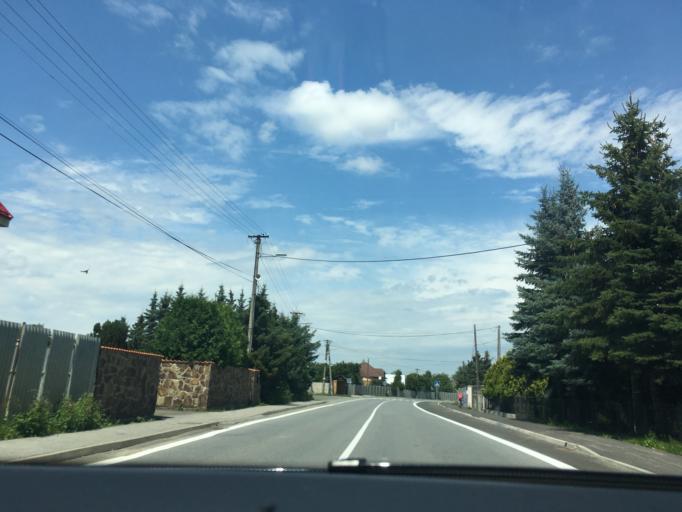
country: SK
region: Presovsky
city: Vranov nad Topl'ou
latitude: 48.8194
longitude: 21.6879
